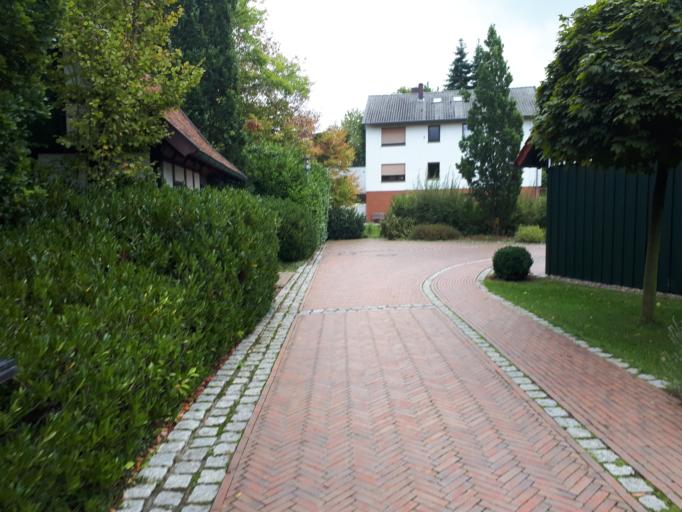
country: DE
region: North Rhine-Westphalia
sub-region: Regierungsbezirk Detmold
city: Huellhorst
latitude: 52.2747
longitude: 8.7131
